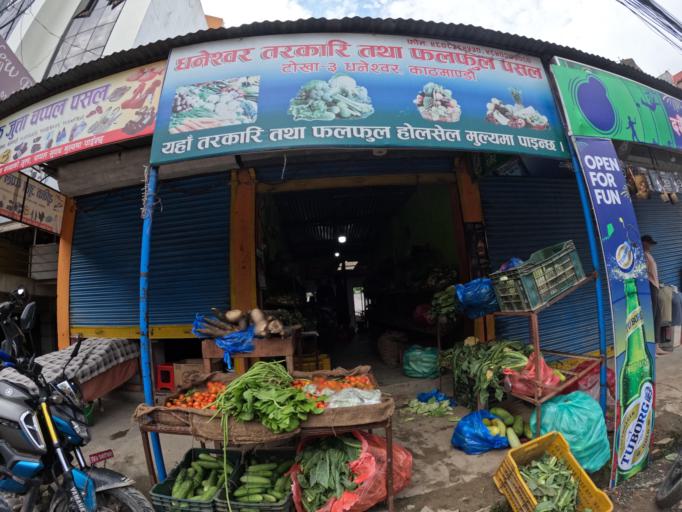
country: NP
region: Central Region
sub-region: Bagmati Zone
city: Kathmandu
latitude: 27.7539
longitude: 85.3184
